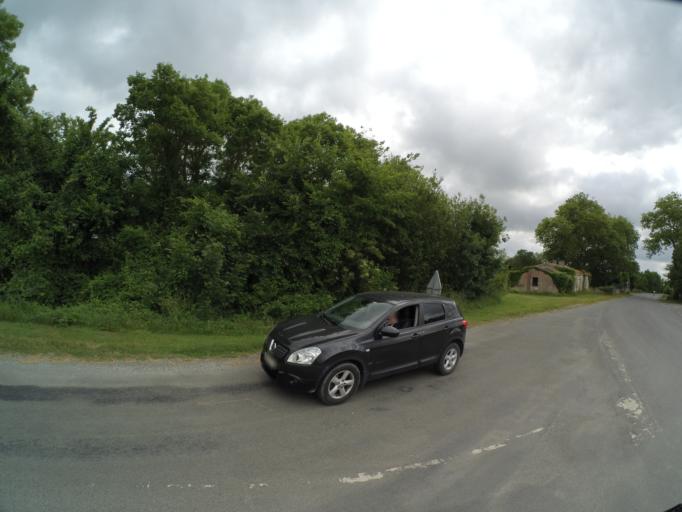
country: FR
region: Poitou-Charentes
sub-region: Departement de la Charente-Maritime
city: Saint-Laurent-de-la-Pree
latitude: 45.9822
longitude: -1.0031
